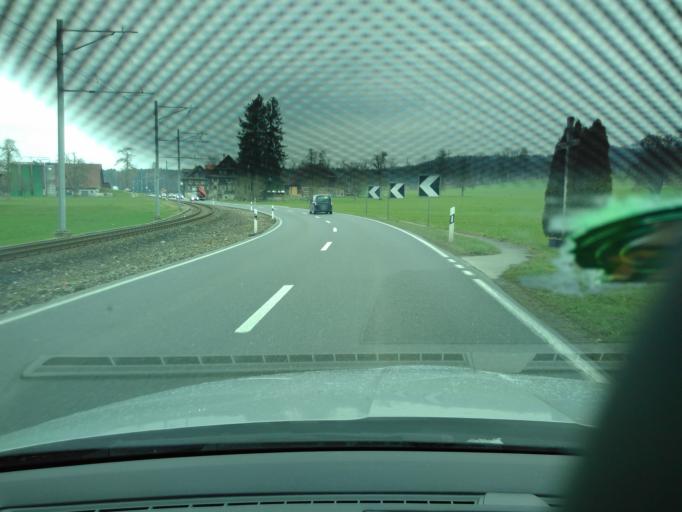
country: CH
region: Lucerne
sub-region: Hochdorf District
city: Hochdorf
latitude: 47.1930
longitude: 8.2800
